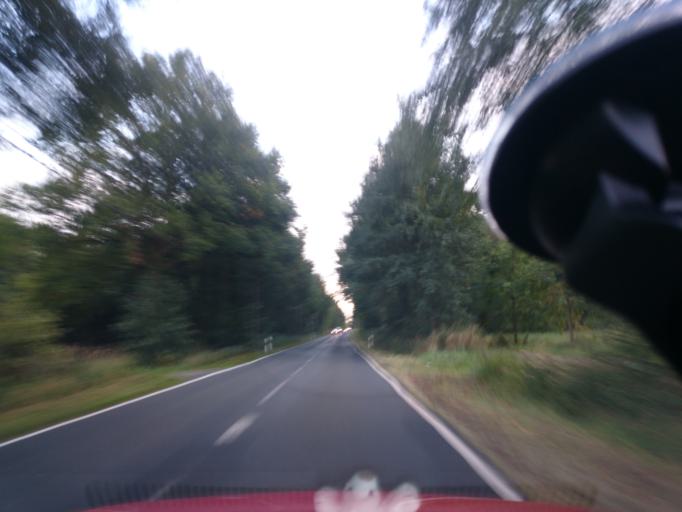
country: DE
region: Mecklenburg-Vorpommern
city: Born
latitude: 54.3495
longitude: 12.5887
